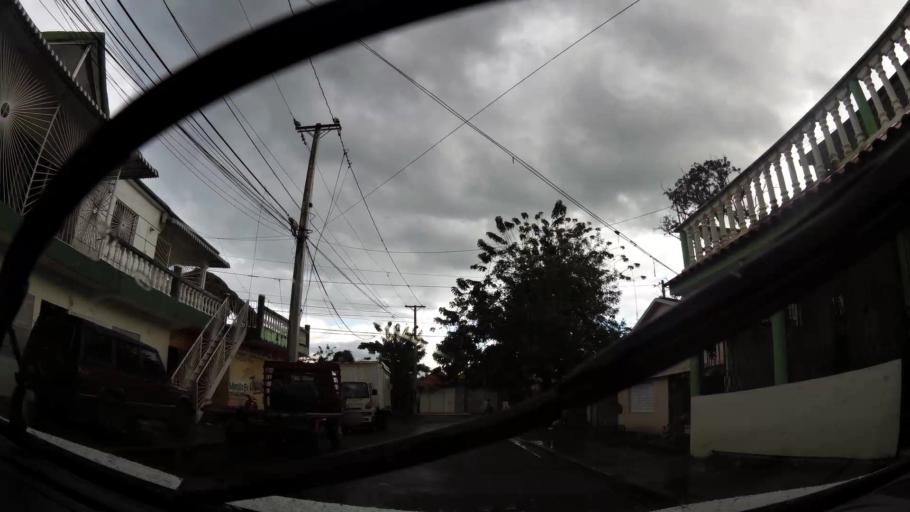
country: DO
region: Monsenor Nouel
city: Bonao
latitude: 18.9428
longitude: -70.4064
